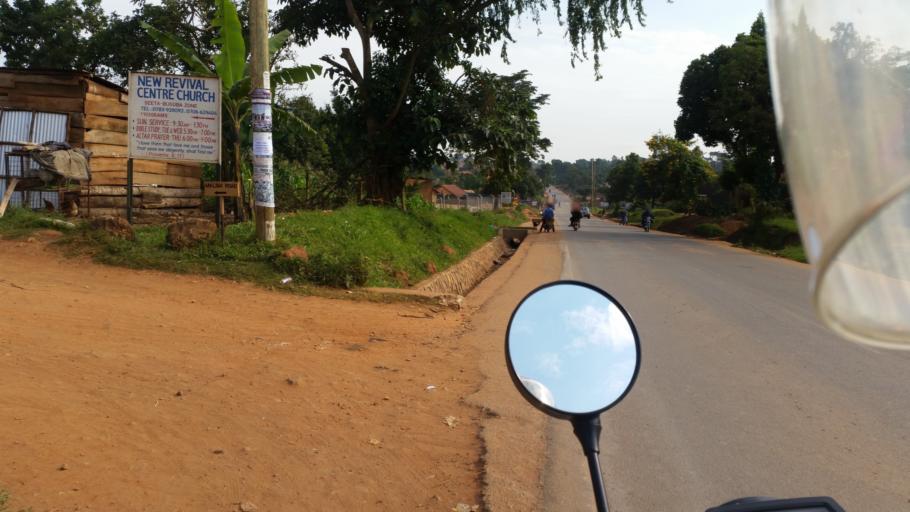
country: UG
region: Central Region
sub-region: Wakiso District
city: Bweyogerere
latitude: 0.3784
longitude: 32.7095
